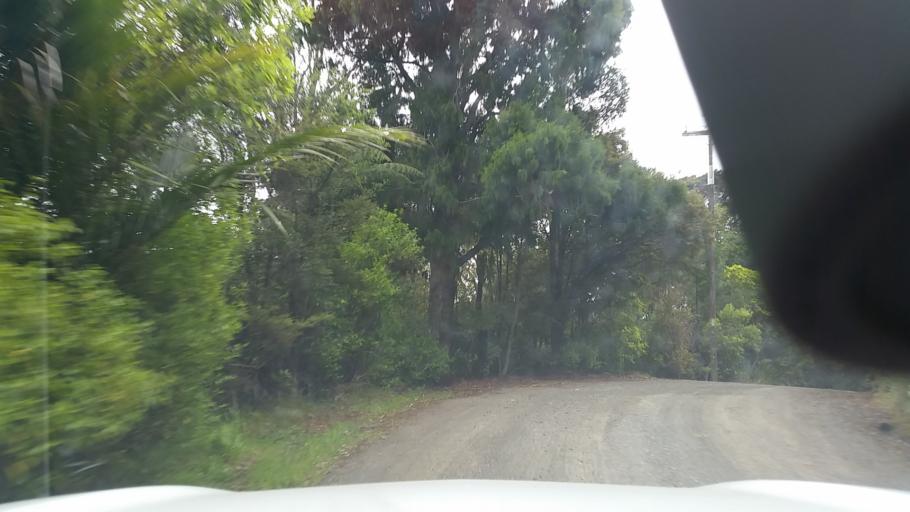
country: NZ
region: Auckland
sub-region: Auckland
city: Muriwai Beach
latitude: -36.8736
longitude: 174.5079
